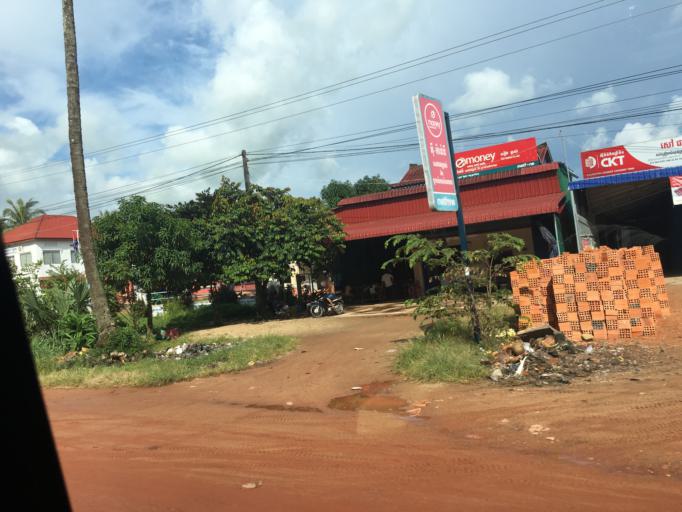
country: KH
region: Preah Sihanouk
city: Sihanoukville
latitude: 10.6311
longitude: 103.7831
